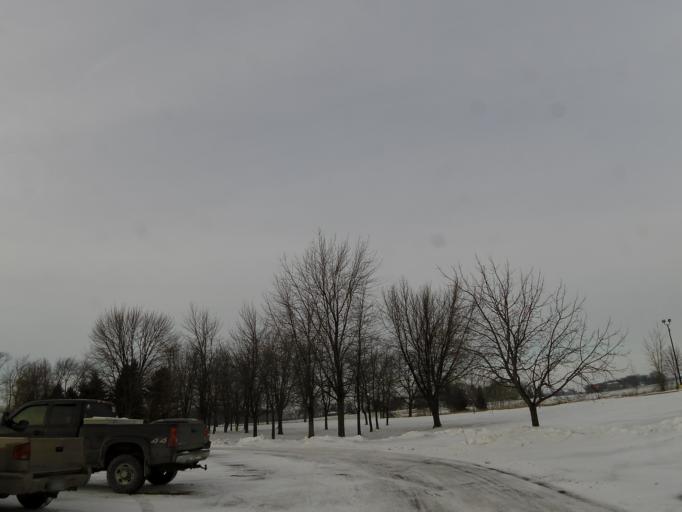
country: US
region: Minnesota
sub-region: McLeod County
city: Hutchinson
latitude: 44.9020
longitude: -94.3537
